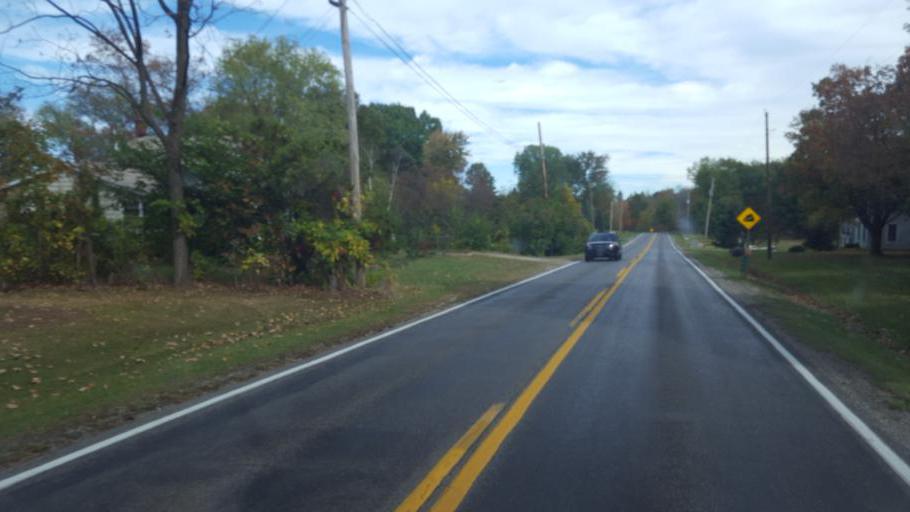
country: US
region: Ohio
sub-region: Lorain County
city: Vermilion-on-the-Lake
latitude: 41.3785
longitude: -82.3195
